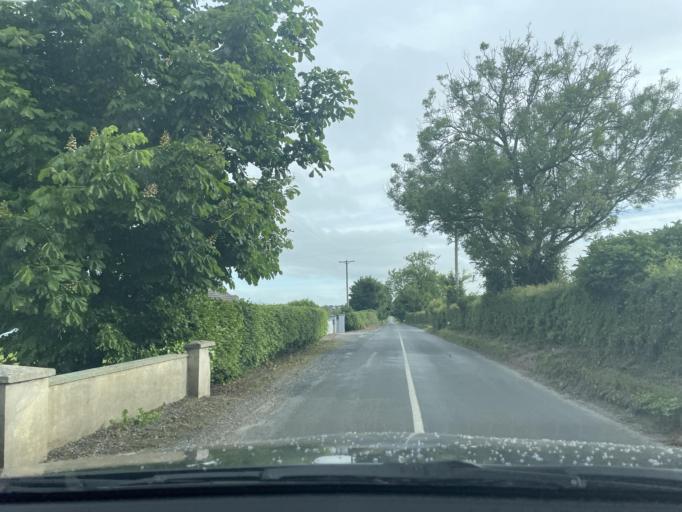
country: IE
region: Leinster
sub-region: County Carlow
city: Bagenalstown
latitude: 52.6409
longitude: -6.9731
